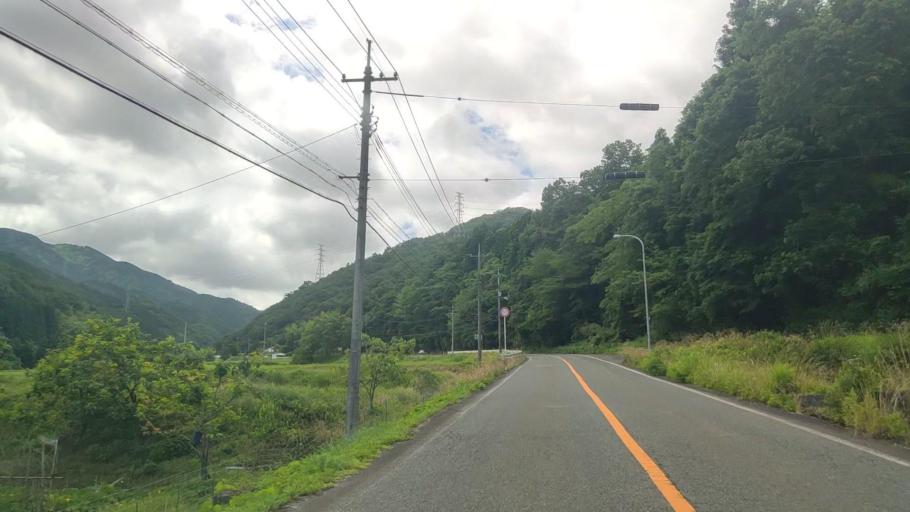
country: JP
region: Tottori
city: Yonago
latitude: 35.2888
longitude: 133.4226
